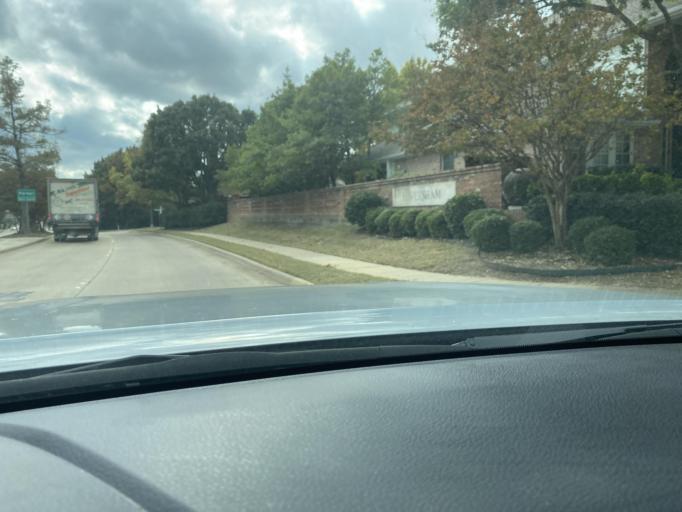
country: US
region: Texas
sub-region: Dallas County
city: Addison
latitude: 33.0447
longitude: -96.7894
